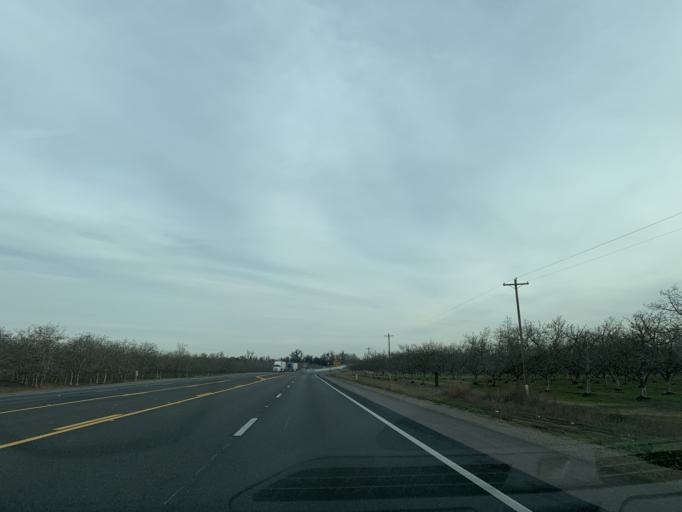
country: US
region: California
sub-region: Yuba County
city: Plumas Lake
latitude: 38.9103
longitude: -121.5972
